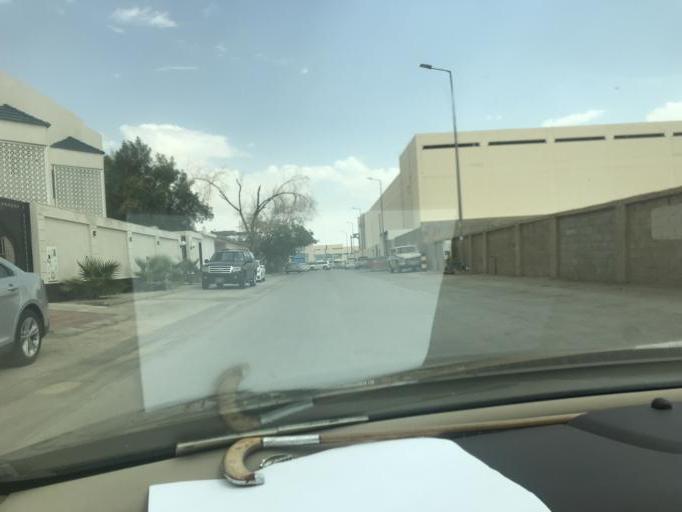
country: SA
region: Ar Riyad
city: Riyadh
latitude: 24.7295
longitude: 46.7815
